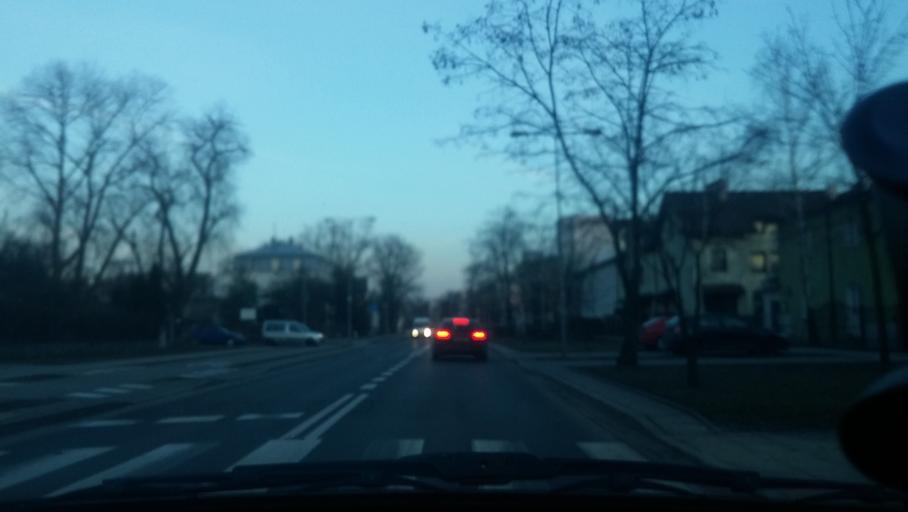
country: PL
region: Masovian Voivodeship
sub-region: Warszawa
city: Praga Poludnie
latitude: 52.2459
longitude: 21.1064
